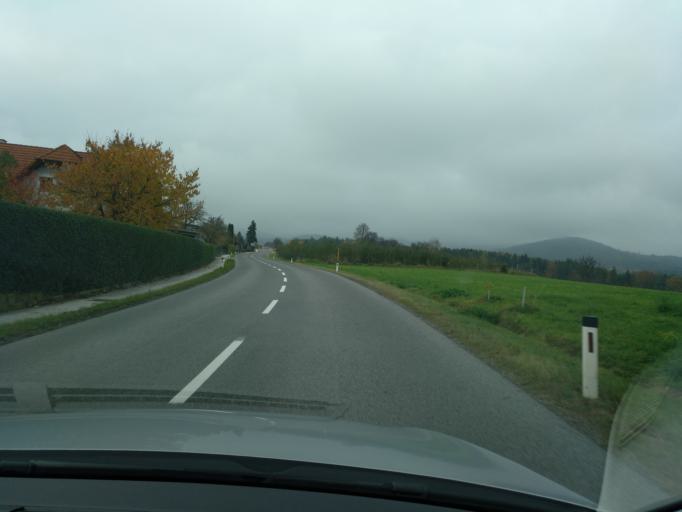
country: AT
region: Styria
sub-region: Politischer Bezirk Hartberg-Fuerstenfeld
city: Rabenwald
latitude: 47.3174
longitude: 15.8123
